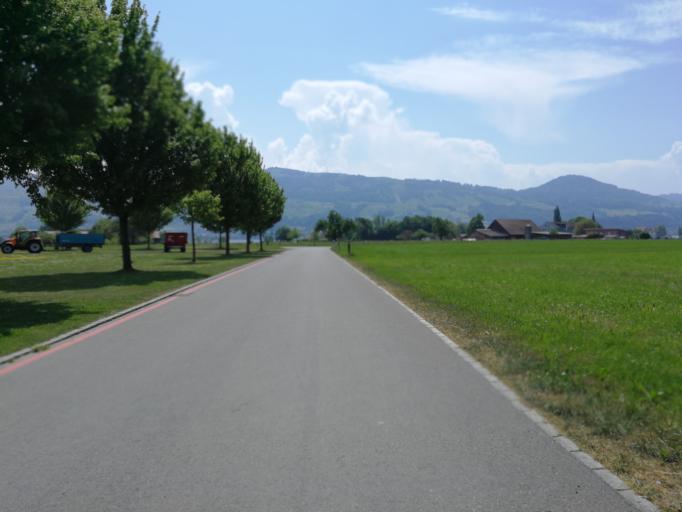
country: CH
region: Saint Gallen
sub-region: Wahlkreis See-Gaster
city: Jona
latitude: 47.2208
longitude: 8.8405
